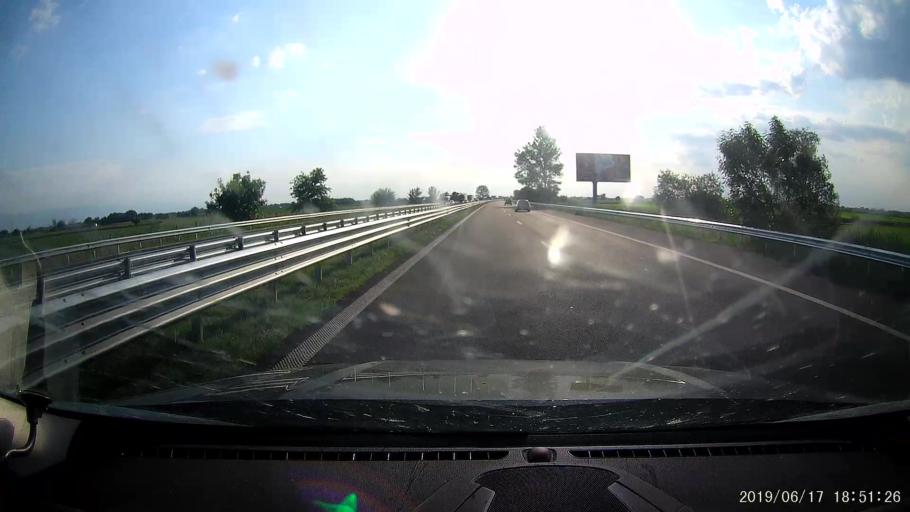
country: BG
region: Plovdiv
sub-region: Obshtina Rakovski
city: Rakovski
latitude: 42.2139
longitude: 24.9715
